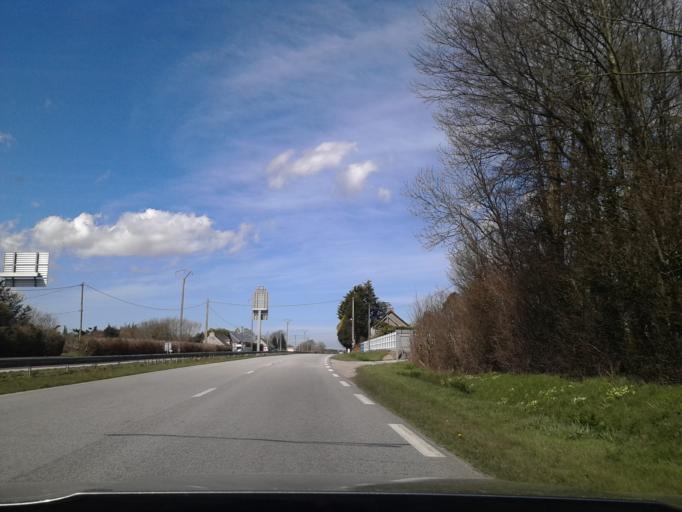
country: FR
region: Lower Normandy
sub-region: Departement de la Manche
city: Brix
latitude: 49.5696
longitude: -1.5743
